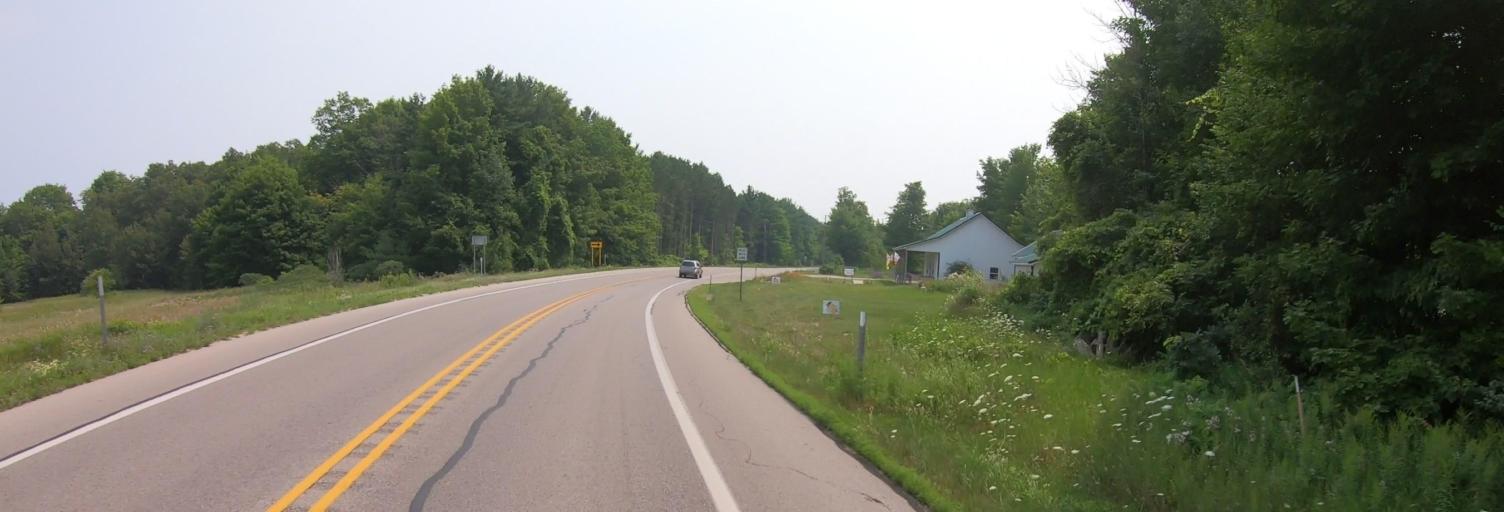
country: US
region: Michigan
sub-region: Leelanau County
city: Leland
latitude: 45.0845
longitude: -85.5962
